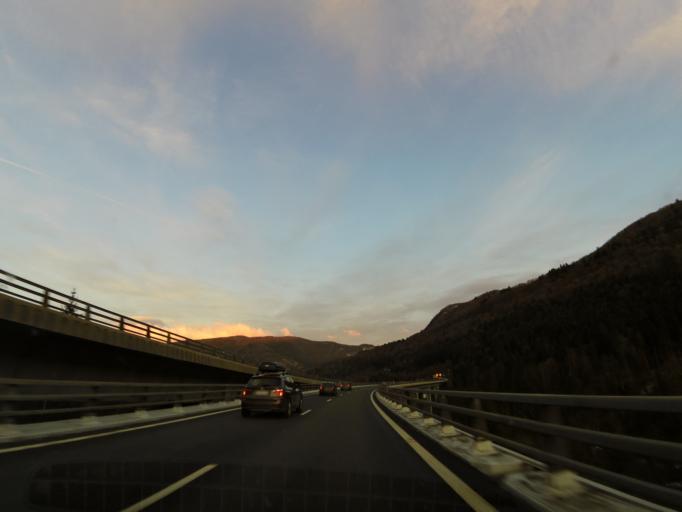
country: FR
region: Rhone-Alpes
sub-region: Departement de l'Ain
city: Chatillon-en-Michaille
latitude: 46.1677
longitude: 5.7153
